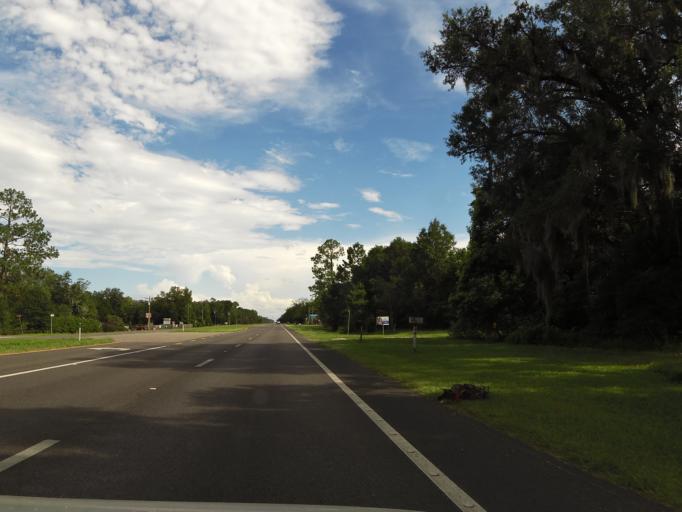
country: US
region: Florida
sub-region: Clay County
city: Green Cove Springs
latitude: 29.9295
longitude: -81.6869
